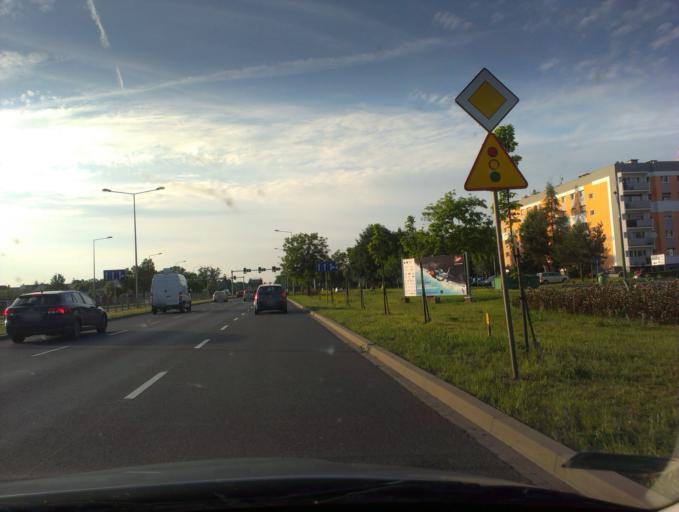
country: PL
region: Greater Poland Voivodeship
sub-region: Leszno
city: Leszno
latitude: 51.8350
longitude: 16.5964
